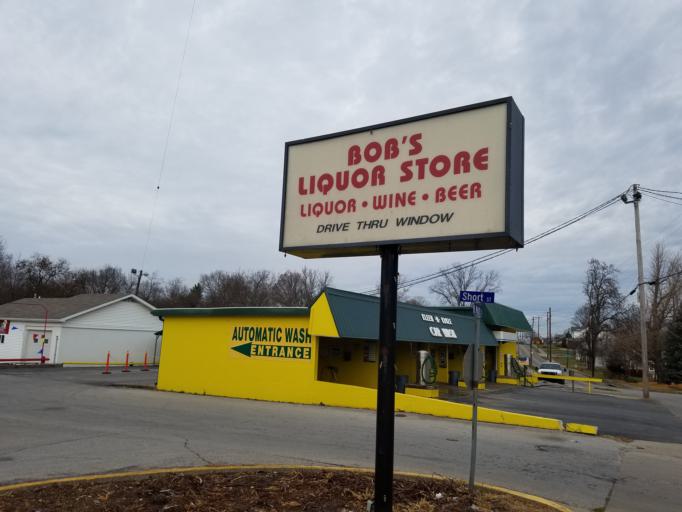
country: US
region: Kentucky
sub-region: Henry County
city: Eminence
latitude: 38.3719
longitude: -85.1793
